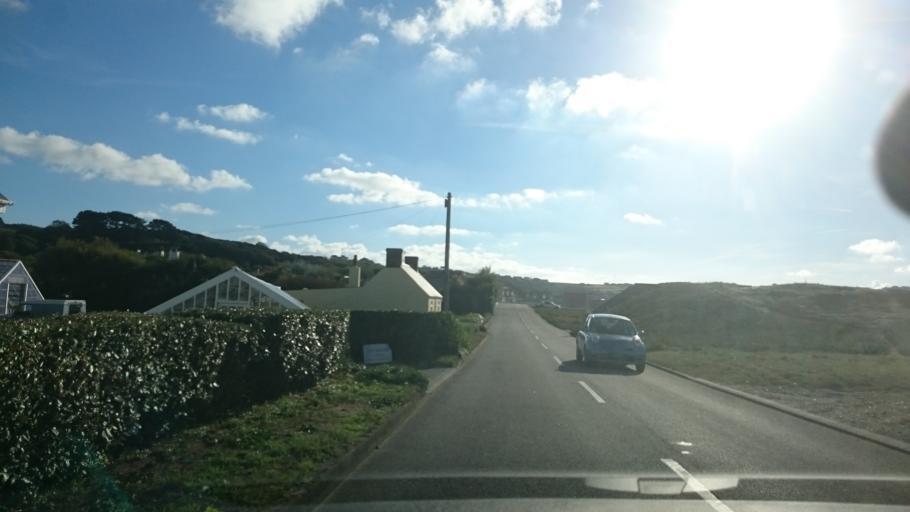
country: GG
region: St Peter Port
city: Saint Peter Port
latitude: 49.4429
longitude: -2.6496
